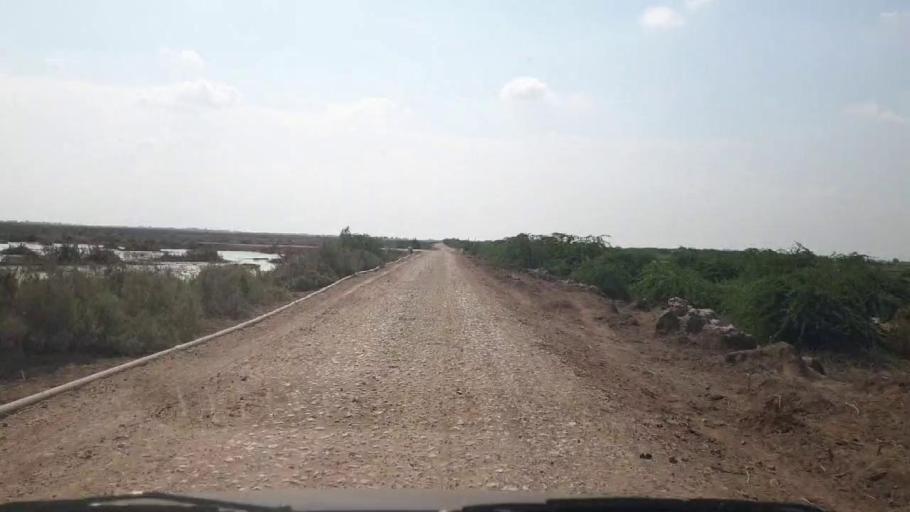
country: PK
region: Sindh
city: Badin
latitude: 24.5077
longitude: 68.6081
